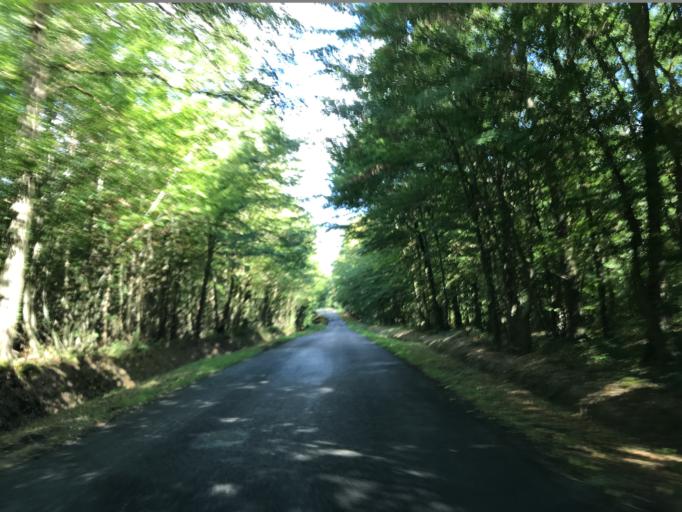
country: FR
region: Haute-Normandie
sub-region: Departement de l'Eure
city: La Chapelle-Reanville
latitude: 49.0859
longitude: 1.3948
